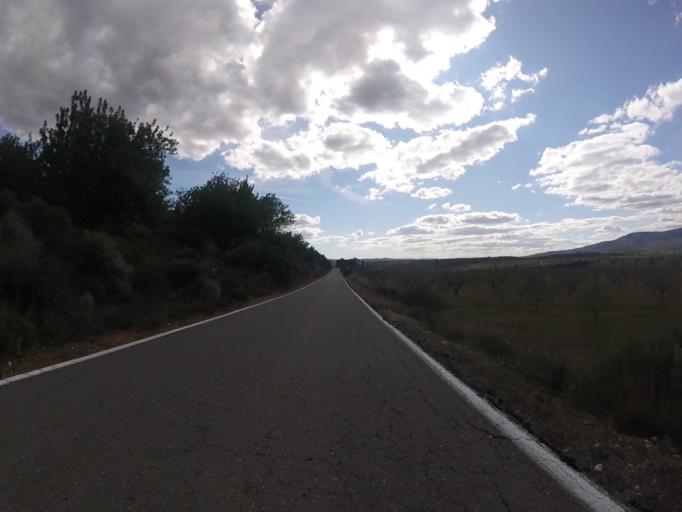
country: ES
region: Valencia
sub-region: Provincia de Castello
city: Cuevas de Vinroma
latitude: 40.3545
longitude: 0.1271
